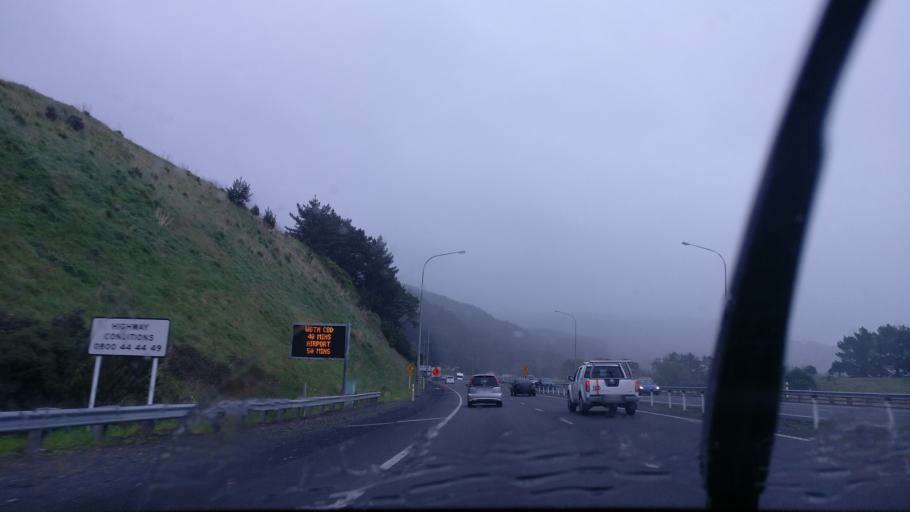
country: NZ
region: Wellington
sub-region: Kapiti Coast District
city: Paraparaumu
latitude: -40.9752
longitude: 174.9794
